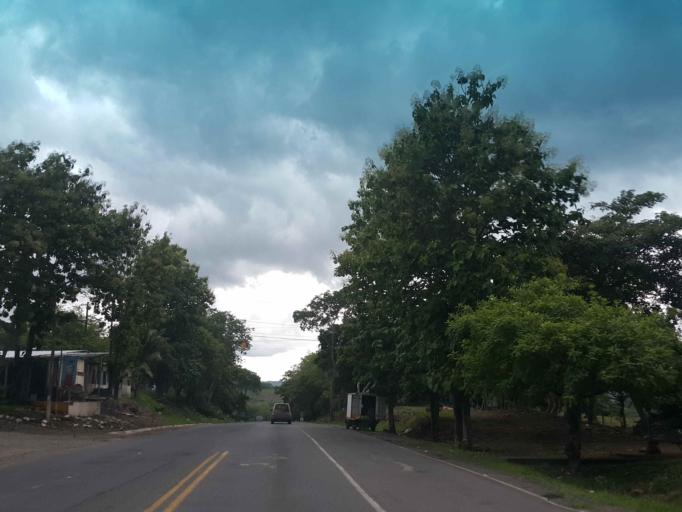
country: CR
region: Puntarenas
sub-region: Canton Central de Puntarenas
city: Chacarita
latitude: 10.0084
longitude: -84.7241
